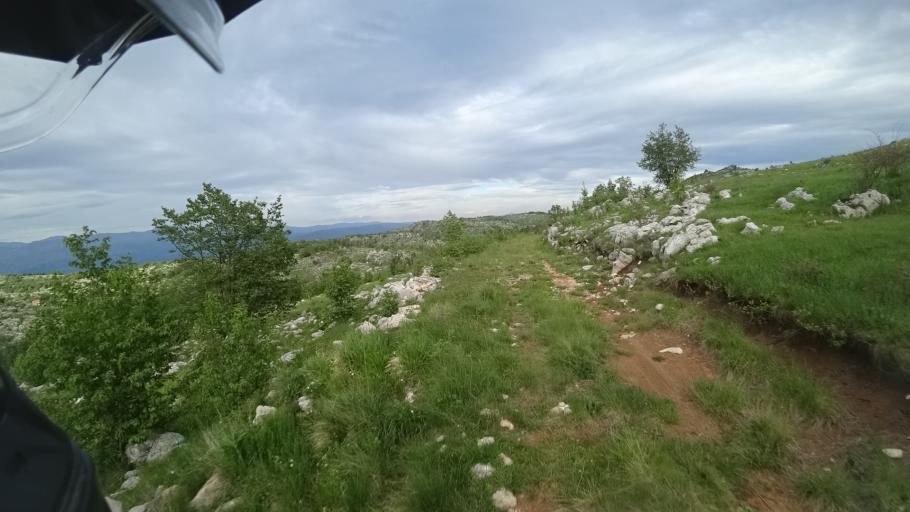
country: HR
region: Sibensko-Kniniska
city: Drnis
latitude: 43.8594
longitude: 16.3890
